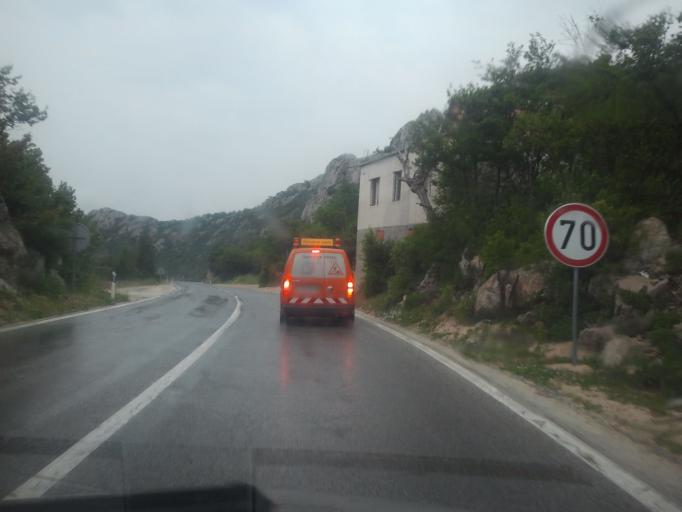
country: HR
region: Zadarska
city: Gracac
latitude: 44.2357
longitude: 15.8152
